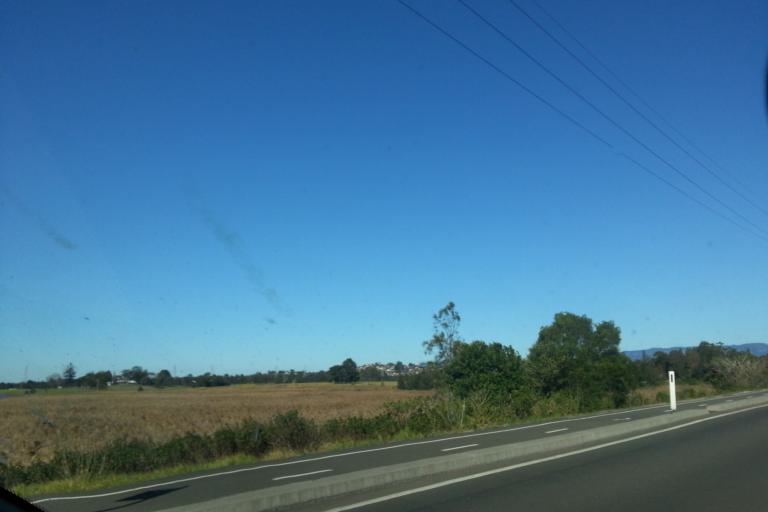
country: AU
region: New South Wales
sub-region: Wollongong
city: Koonawarra
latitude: -34.4717
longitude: 150.8166
